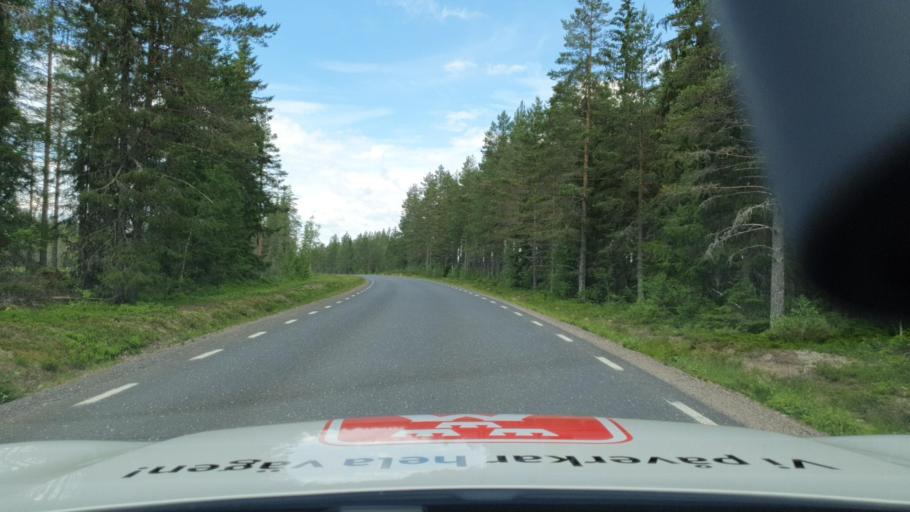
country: SE
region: Vaermland
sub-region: Torsby Kommun
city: Torsby
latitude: 60.5419
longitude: 12.7989
